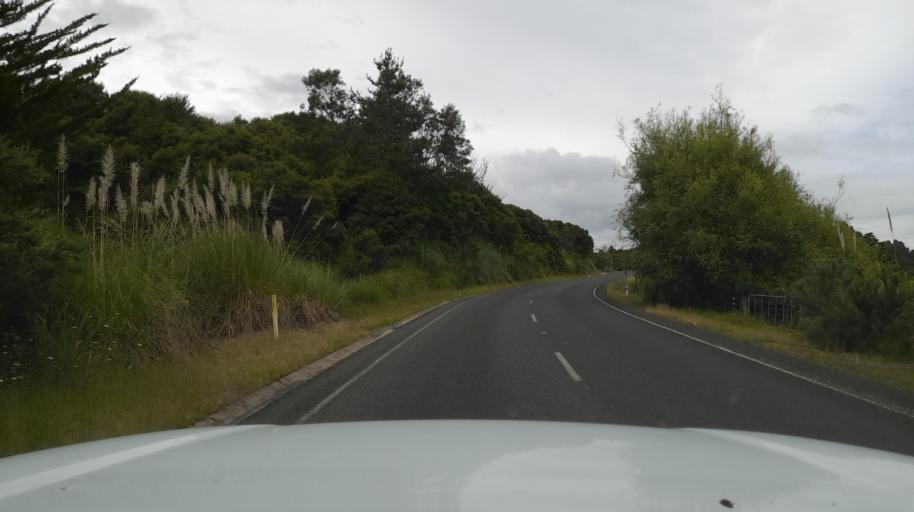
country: NZ
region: Northland
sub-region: Far North District
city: Kaitaia
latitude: -35.3607
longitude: 173.4026
